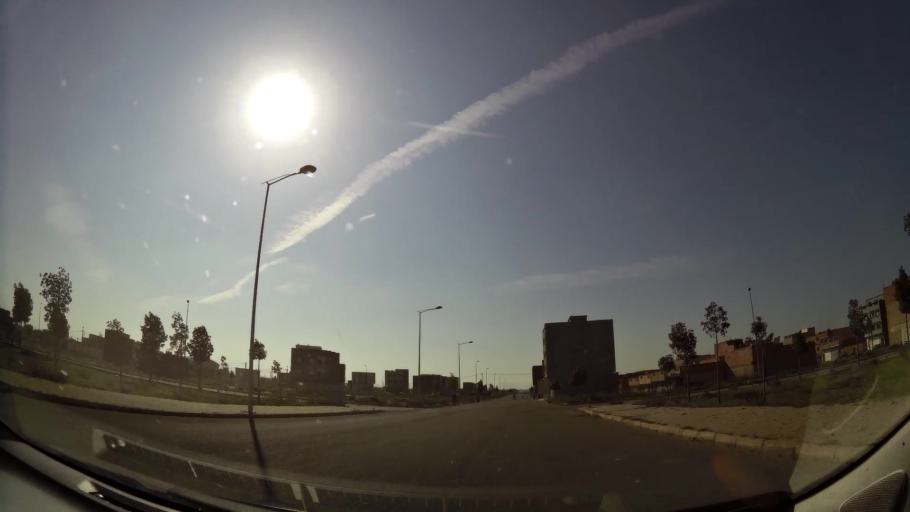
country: MA
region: Oriental
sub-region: Oujda-Angad
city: Oujda
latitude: 34.7170
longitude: -1.8835
